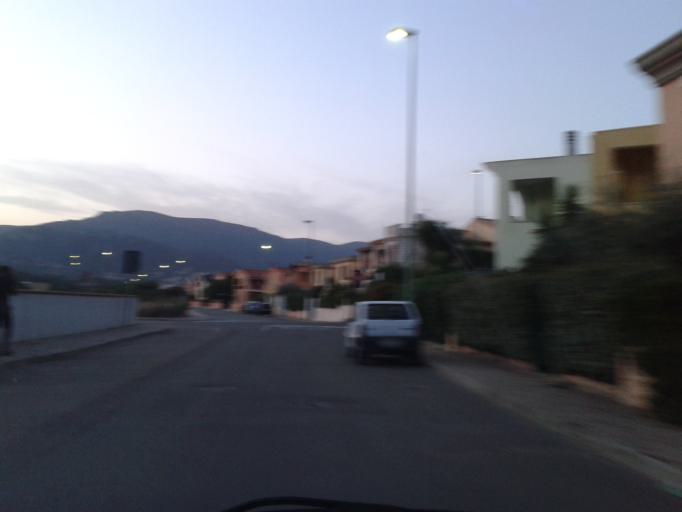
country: IT
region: Sardinia
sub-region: Provincia di Cagliari
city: Villasimius
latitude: 39.1497
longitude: 9.5176
